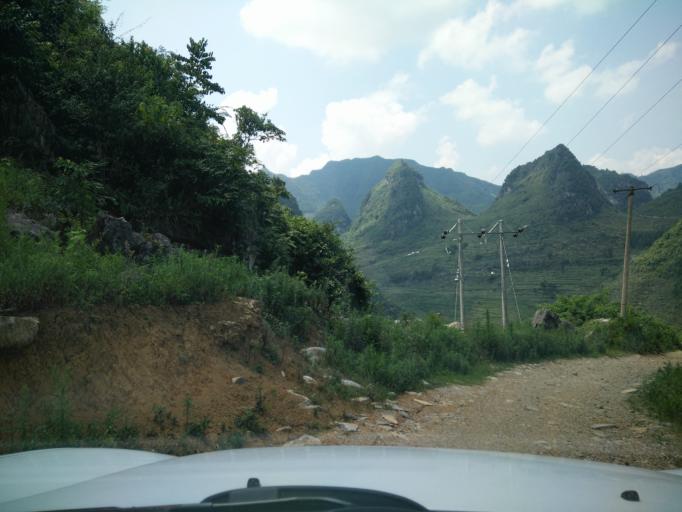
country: CN
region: Guangxi Zhuangzu Zizhiqu
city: Xinzhou
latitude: 25.0050
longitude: 105.7035
